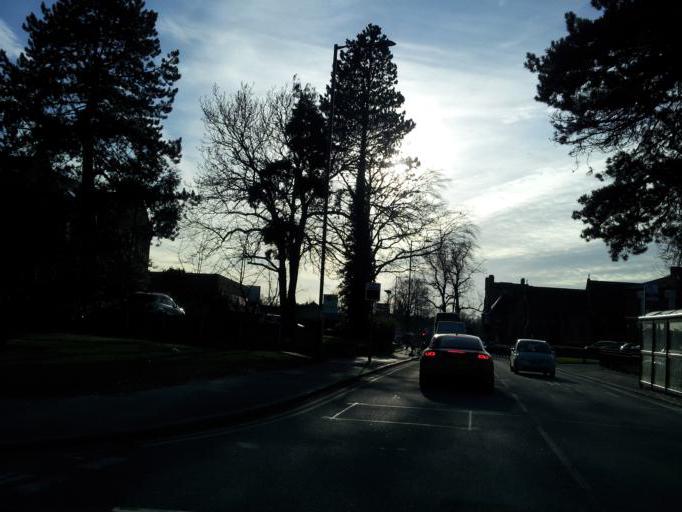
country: GB
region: England
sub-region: City and Borough of Birmingham
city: Sutton Coldfield
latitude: 52.5291
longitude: -1.8345
